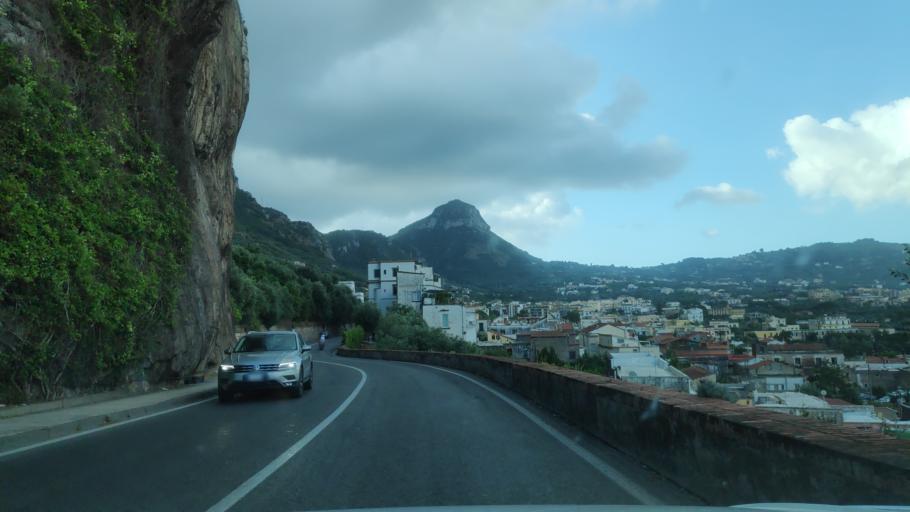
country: IT
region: Campania
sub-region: Provincia di Napoli
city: Meta
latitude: 40.6454
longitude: 14.4141
